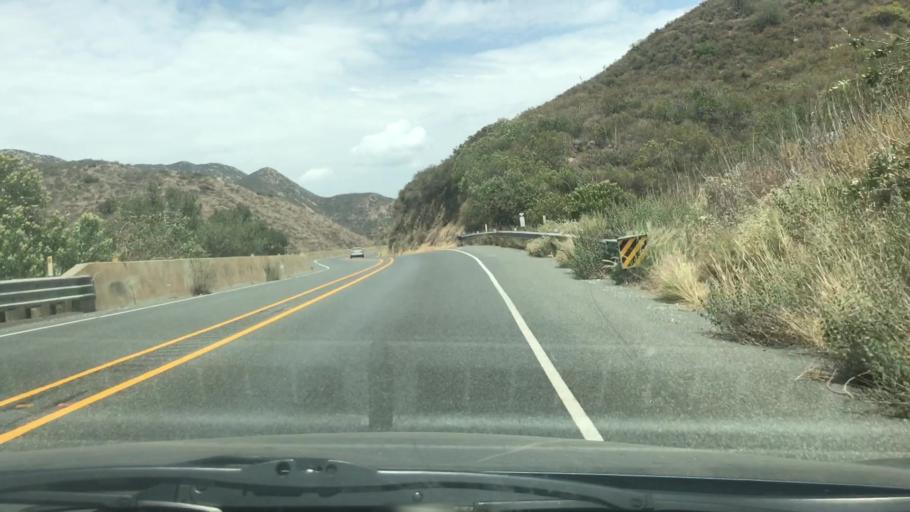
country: US
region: California
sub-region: Orange County
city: Coto De Caza
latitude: 33.5927
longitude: -117.4959
